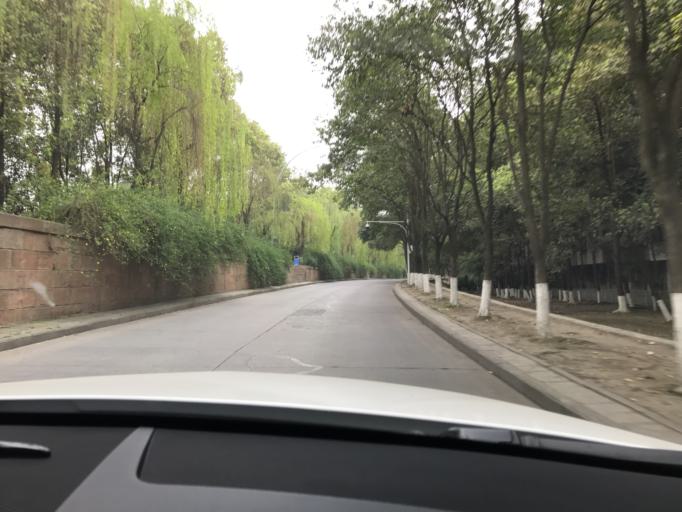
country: CN
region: Sichuan
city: Mianyang
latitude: 31.4509
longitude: 104.7579
